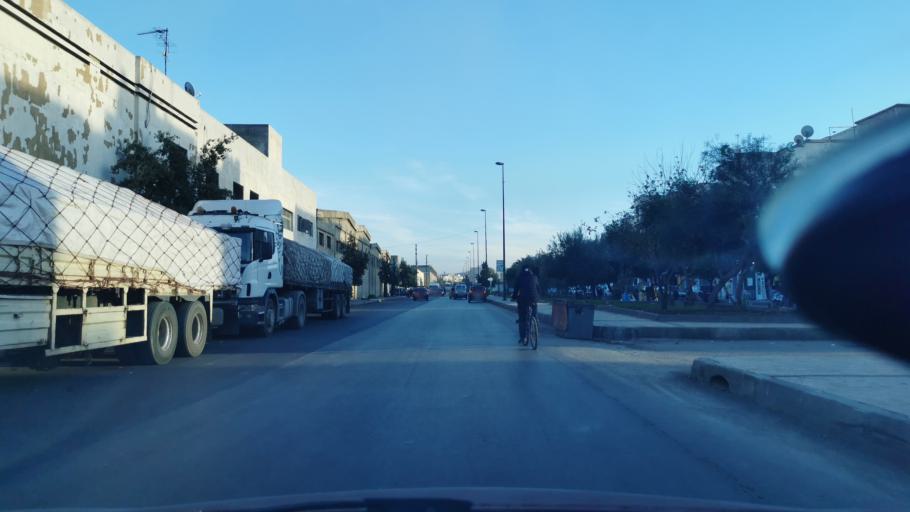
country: MA
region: Fes-Boulemane
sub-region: Fes
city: Fes
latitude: 34.0252
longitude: -4.9855
